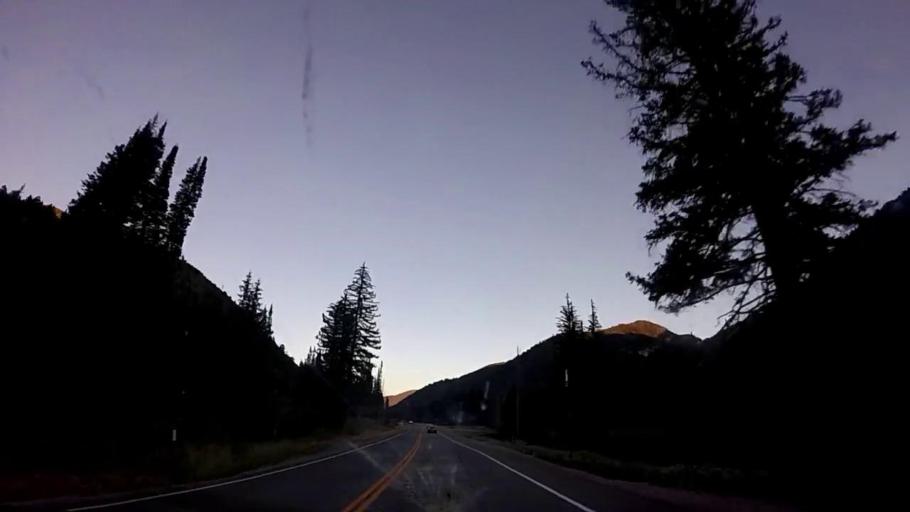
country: US
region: Utah
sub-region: Summit County
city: Summit Park
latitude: 40.6453
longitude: -111.6421
